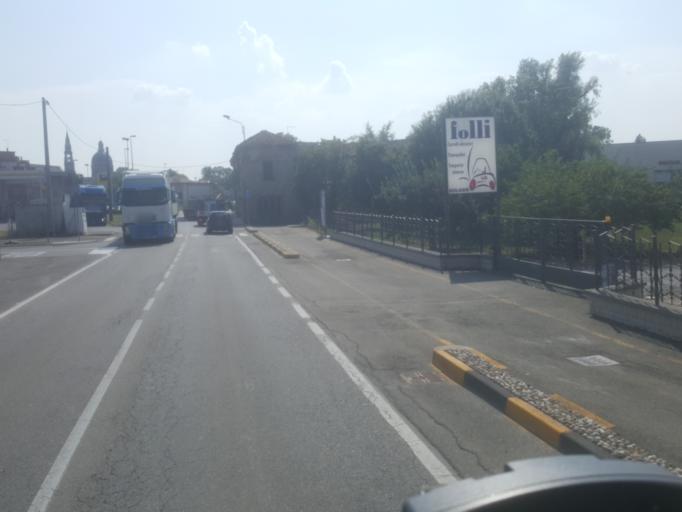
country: IT
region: Lombardy
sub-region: Provincia di Cremona
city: Casalmaggiore
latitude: 44.9950
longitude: 10.4189
